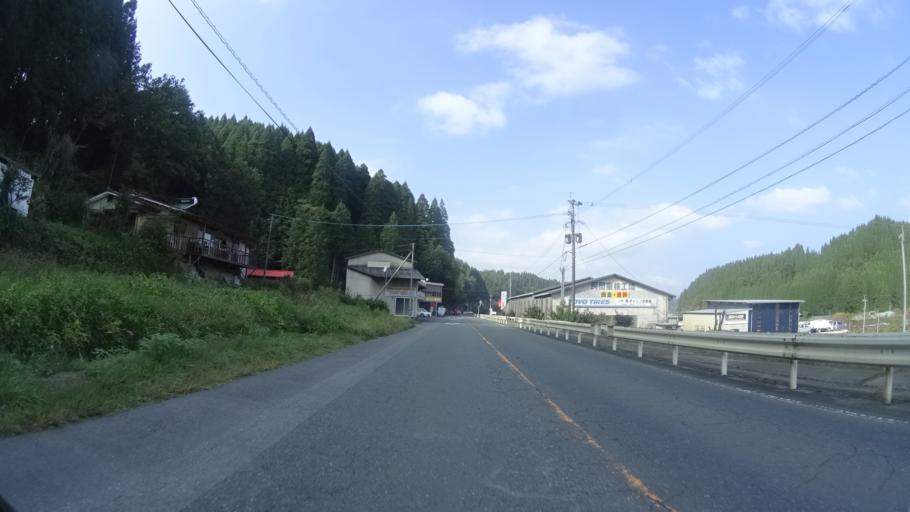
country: JP
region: Kumamoto
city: Aso
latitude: 33.0899
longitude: 131.0676
